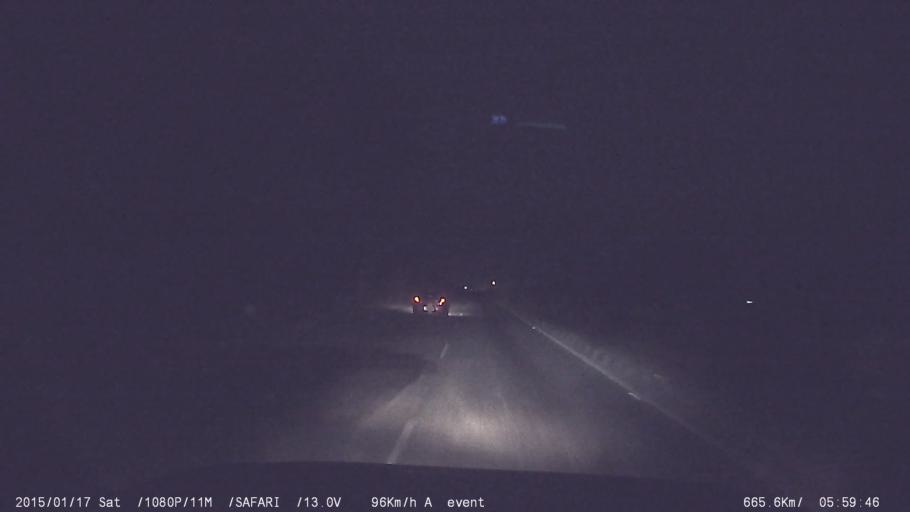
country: IN
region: Tamil Nadu
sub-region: Kancheepuram
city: Kanchipuram
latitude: 12.8972
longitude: 79.5701
